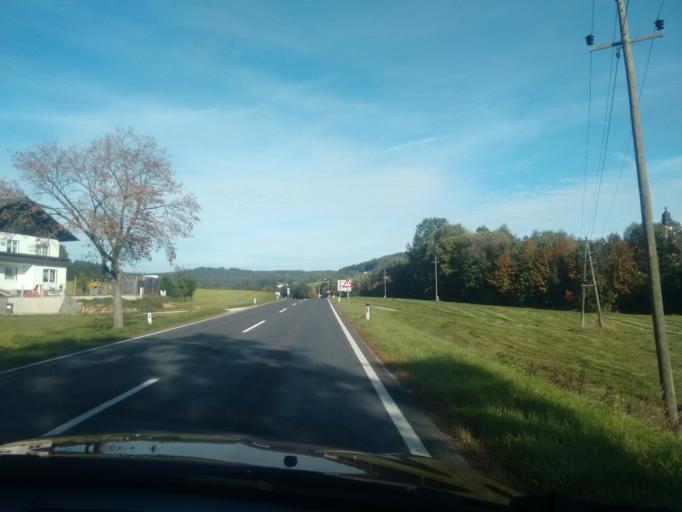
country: AT
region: Upper Austria
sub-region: Politischer Bezirk Vocklabruck
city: Zell am Pettenfirst
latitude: 48.0744
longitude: 13.5976
